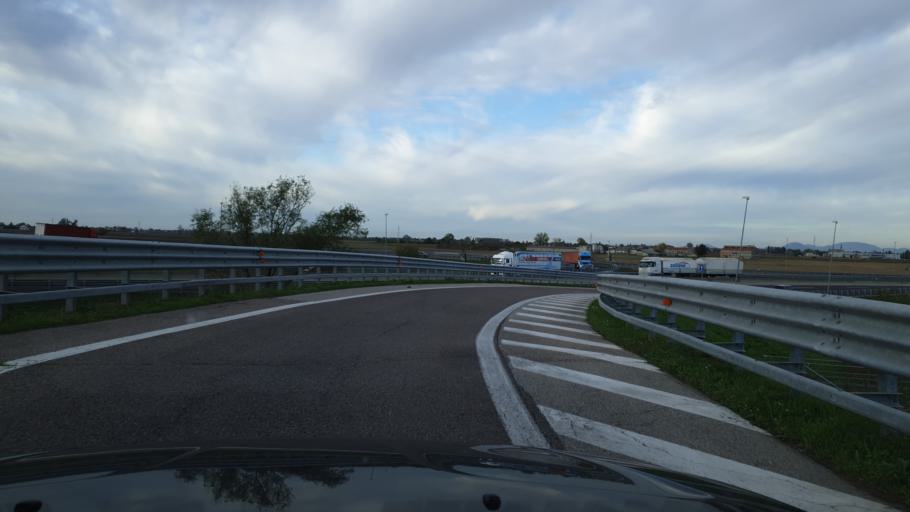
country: IT
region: Veneto
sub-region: Provincia di Rovigo
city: Villamarzana
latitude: 45.0233
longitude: 11.6960
